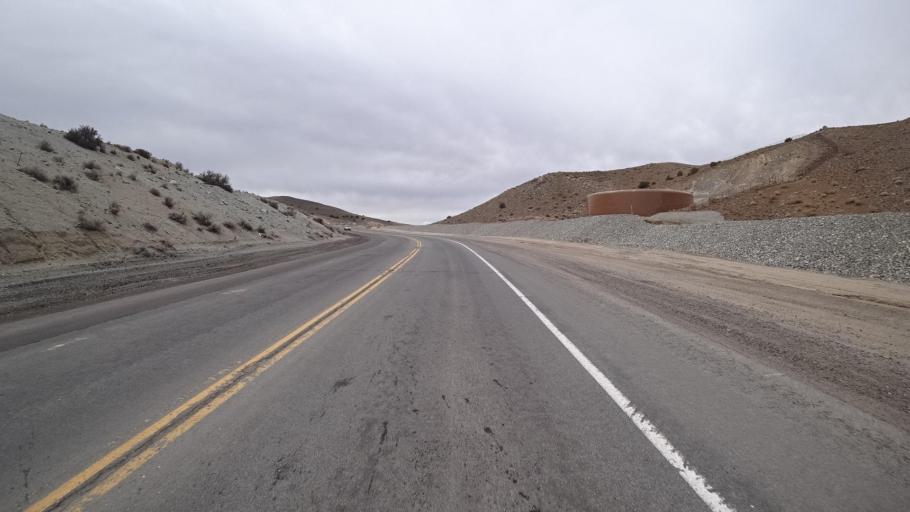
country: US
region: Nevada
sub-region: Washoe County
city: Sun Valley
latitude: 39.6109
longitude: -119.7383
